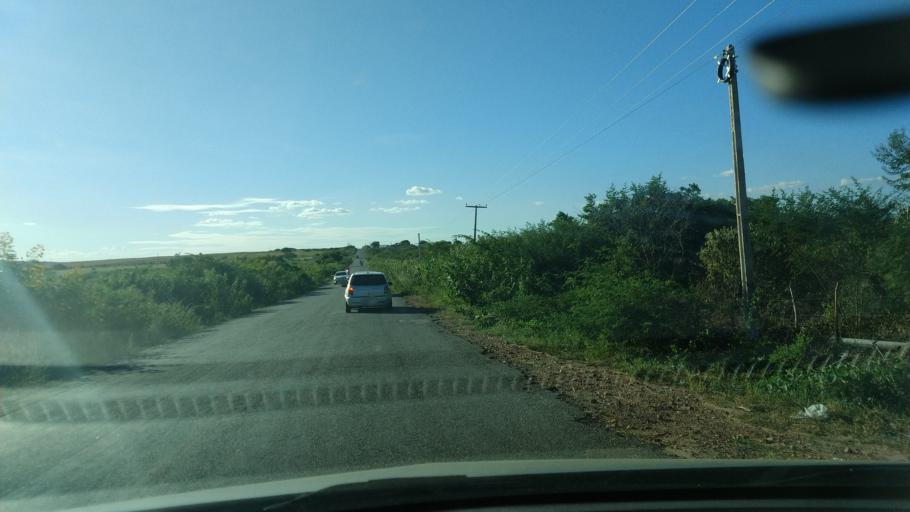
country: BR
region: Rio Grande do Norte
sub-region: Sao Jose Do Campestre
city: Sao Jose do Campestre
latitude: -6.4147
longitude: -35.6507
